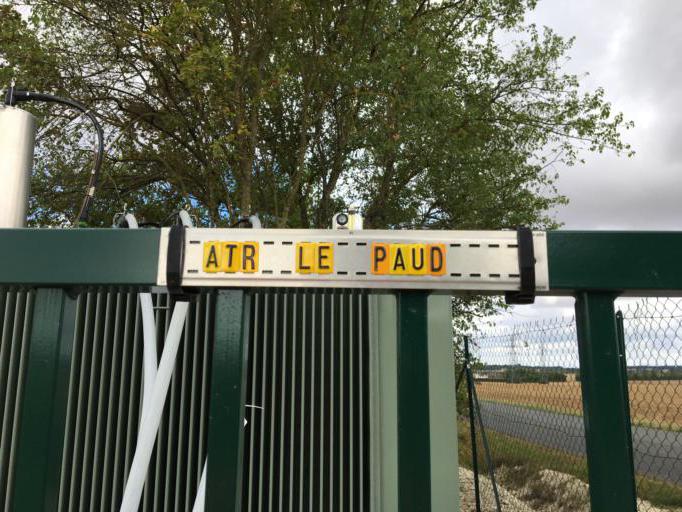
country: FR
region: Poitou-Charentes
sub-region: Departement de la Charente-Maritime
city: Saint-Georges-du-Bois
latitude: 46.0998
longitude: -0.6594
